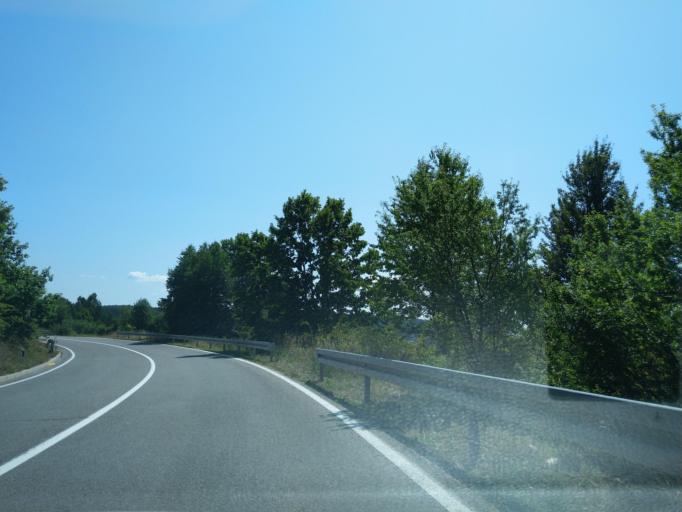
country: RS
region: Central Serbia
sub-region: Zlatiborski Okrug
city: Sjenica
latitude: 43.3065
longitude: 19.9196
